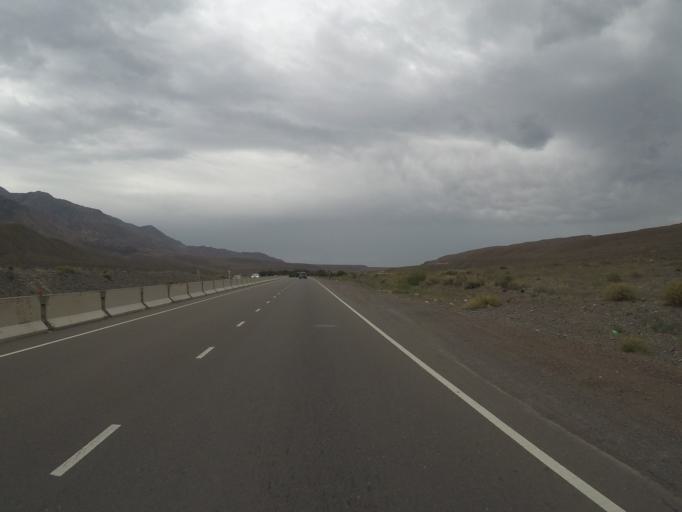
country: KG
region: Ysyk-Koel
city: Balykchy
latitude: 42.4665
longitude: 75.9467
